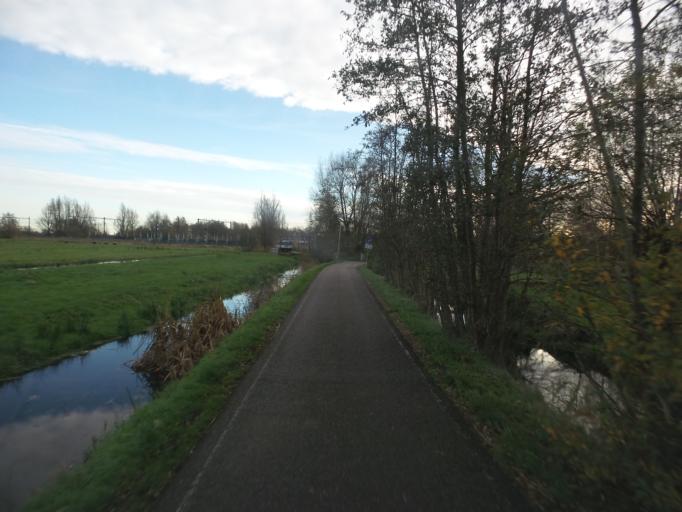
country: NL
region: South Holland
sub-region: Gemeente Vlist
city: Haastrecht
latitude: 52.0158
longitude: 4.7496
